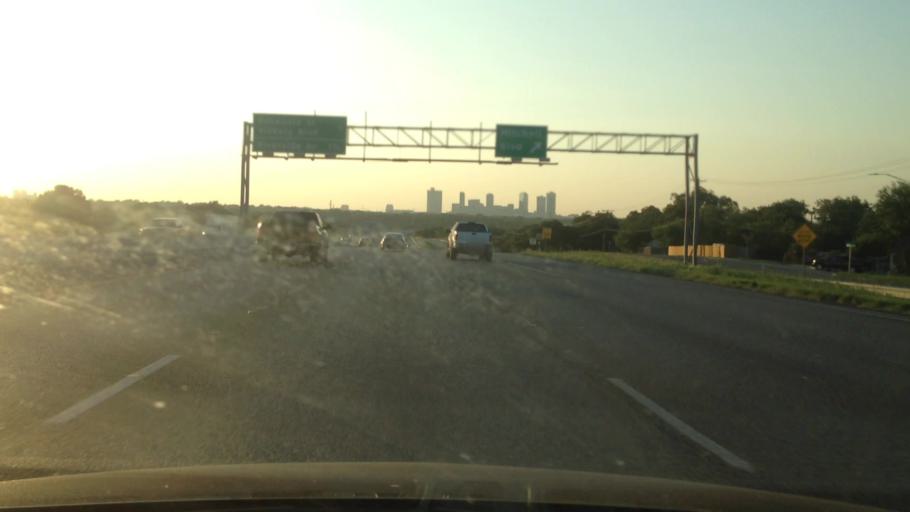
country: US
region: Texas
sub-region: Tarrant County
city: Fort Worth
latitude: 32.7172
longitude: -97.2851
